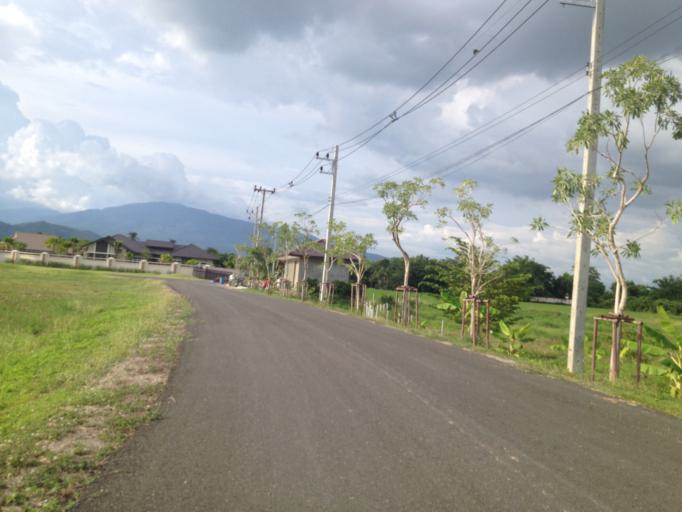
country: TH
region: Chiang Mai
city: Hang Dong
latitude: 18.7093
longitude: 98.9175
